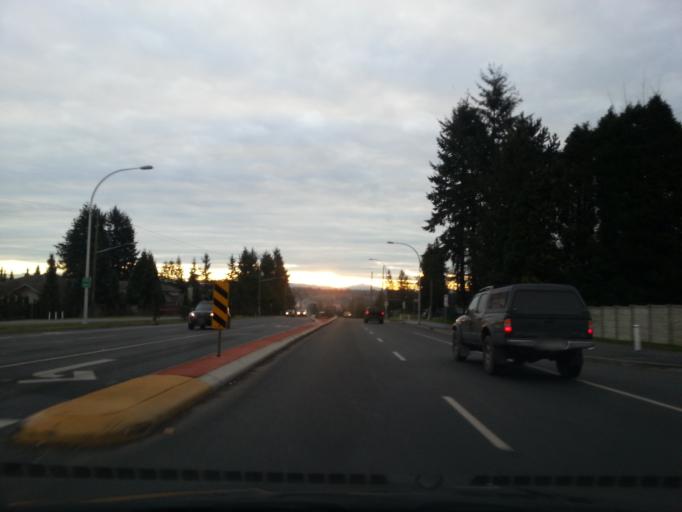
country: CA
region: British Columbia
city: Surrey
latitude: 49.1478
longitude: -122.7564
